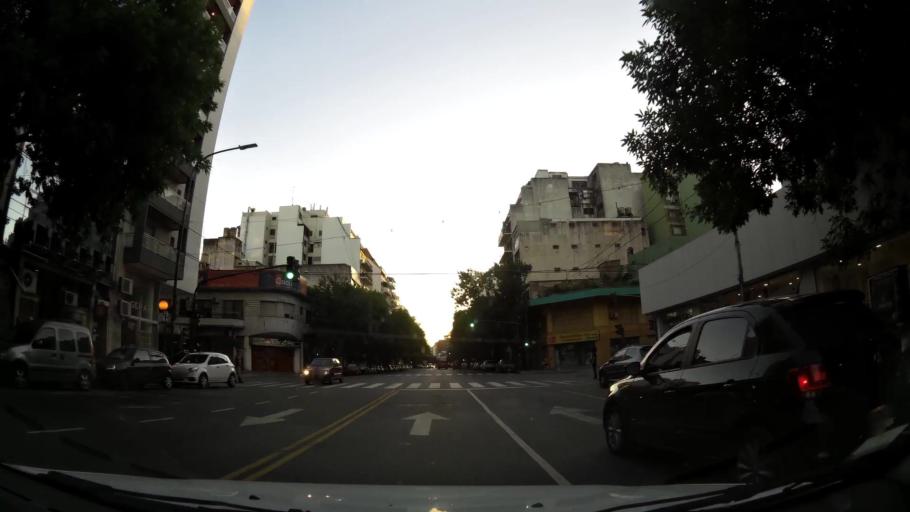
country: AR
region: Buenos Aires F.D.
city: Colegiales
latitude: -34.6005
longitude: -58.4397
